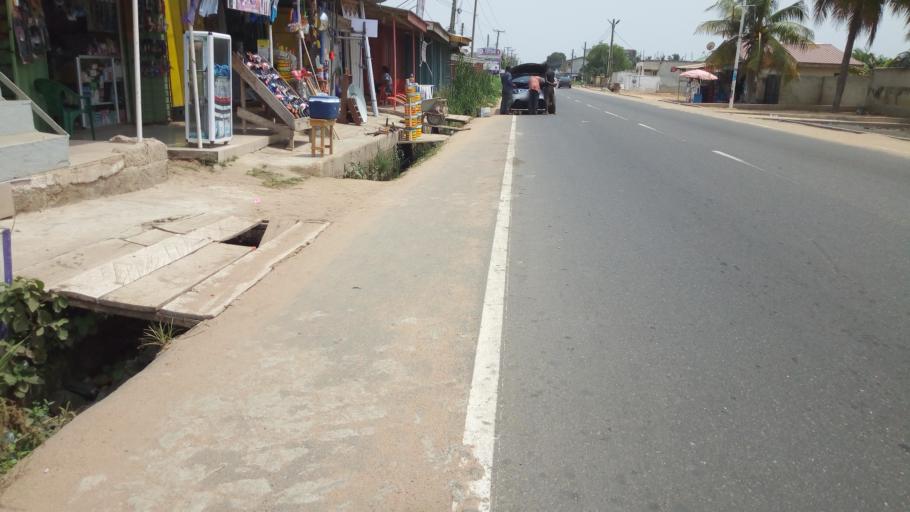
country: GH
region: Greater Accra
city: Gbawe
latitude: 5.5580
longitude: -0.3082
